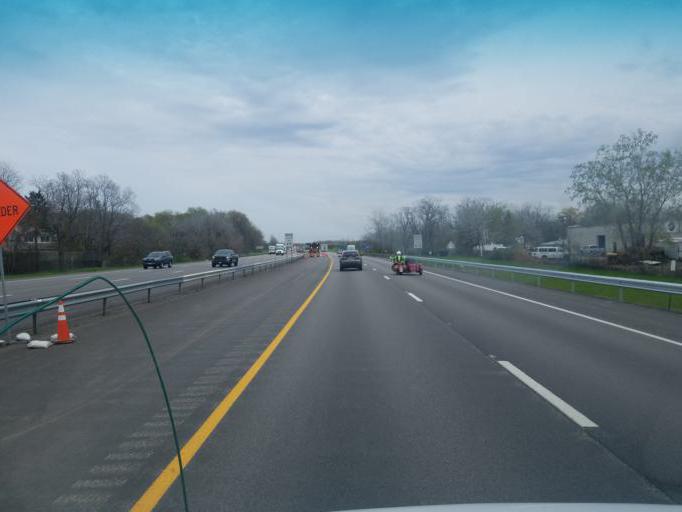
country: US
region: New York
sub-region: Erie County
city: Williamsville
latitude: 42.9507
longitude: -78.7343
